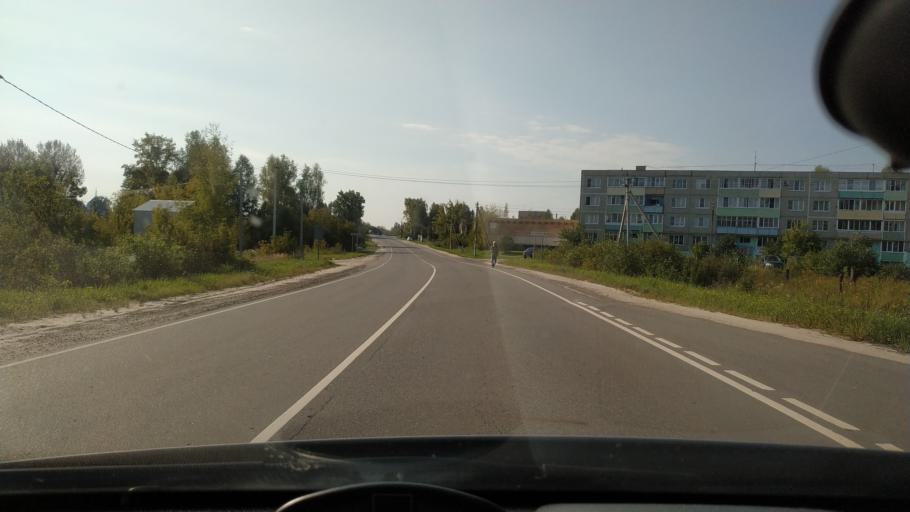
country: RU
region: Moskovskaya
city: Dmitrovskiy Pogost
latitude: 55.3214
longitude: 39.8255
